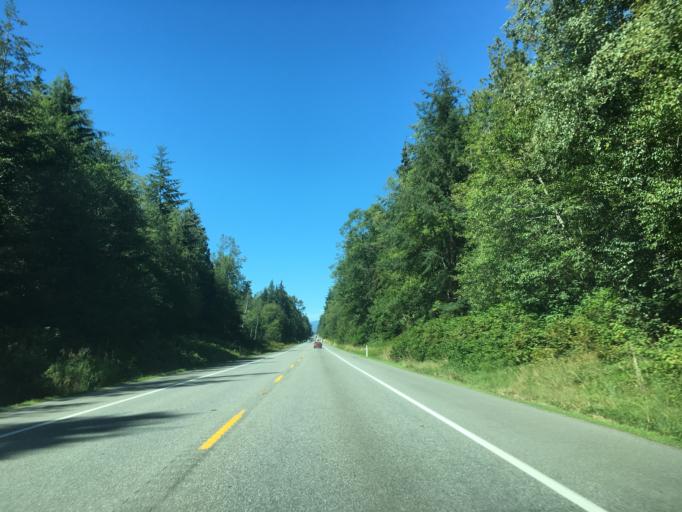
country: US
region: Washington
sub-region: Snohomish County
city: Sisco Heights
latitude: 48.1003
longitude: -122.1120
